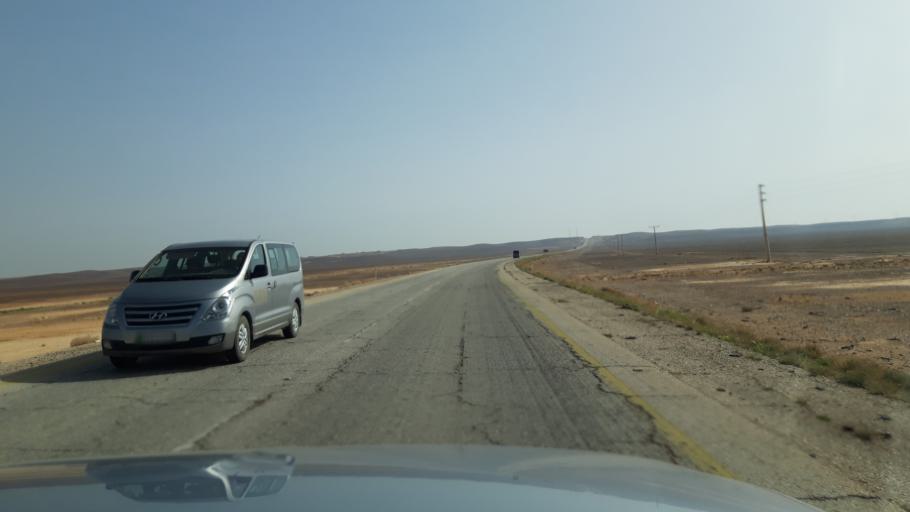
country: JO
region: Amman
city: Al Azraq ash Shamali
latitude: 31.8429
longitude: 36.6469
